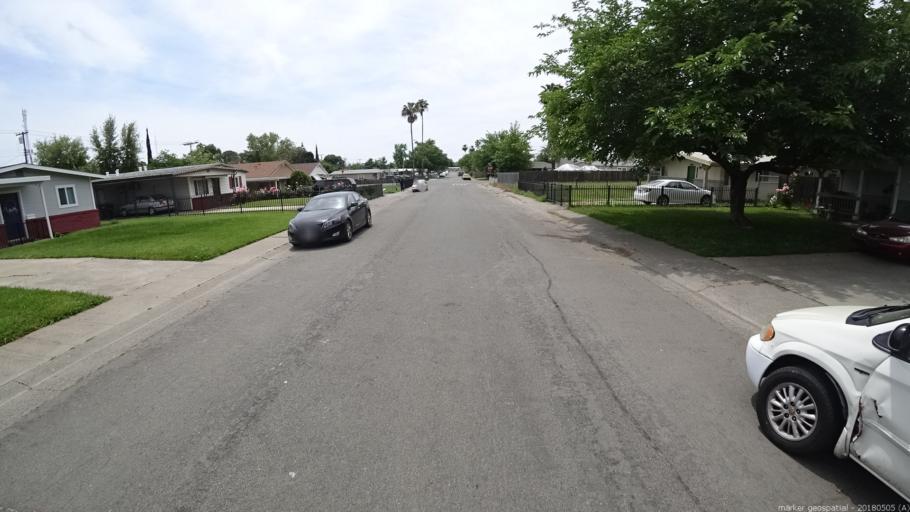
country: US
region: California
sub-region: Sacramento County
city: Rio Linda
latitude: 38.6390
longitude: -121.4373
